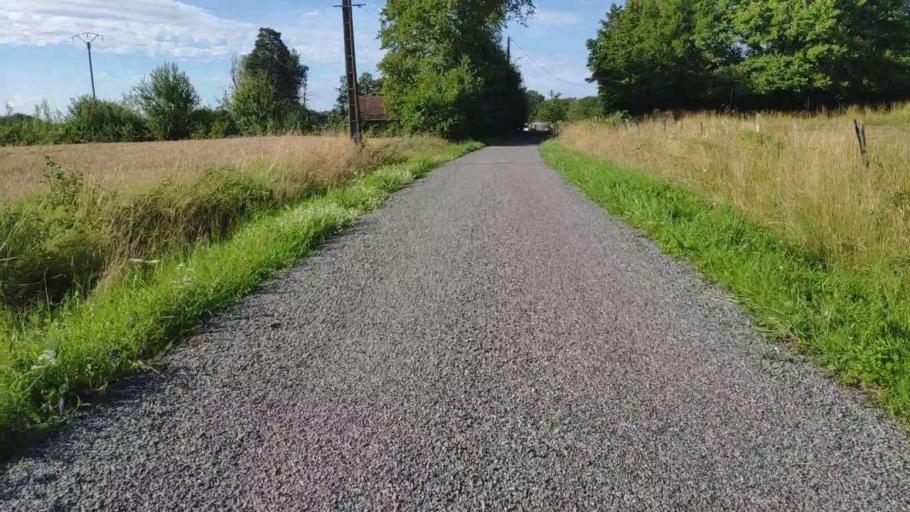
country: FR
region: Franche-Comte
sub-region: Departement du Jura
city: Bletterans
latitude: 46.8320
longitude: 5.5014
